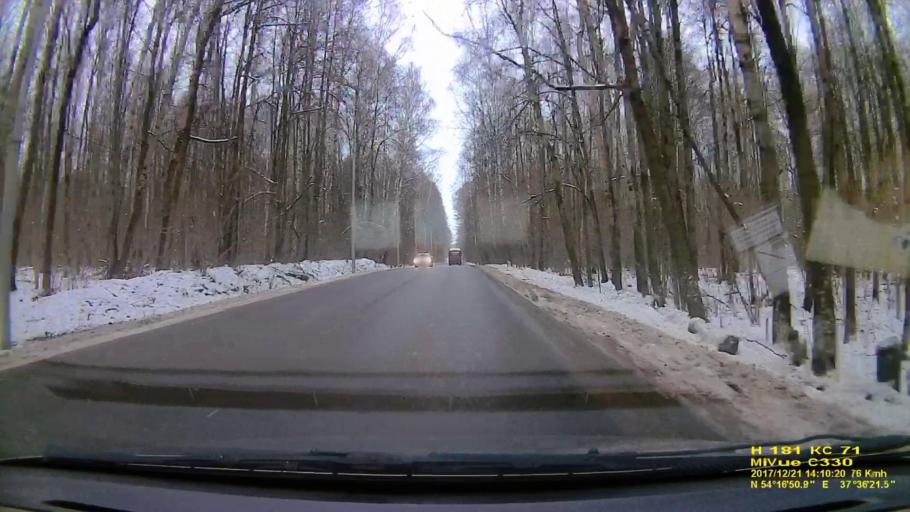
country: RU
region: Tula
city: Gorelki
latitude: 54.2807
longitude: 37.6060
